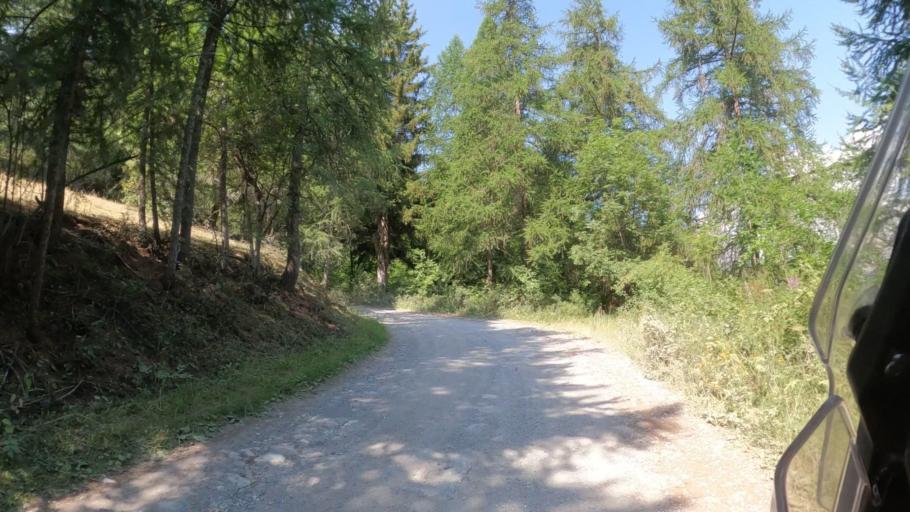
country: IT
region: Piedmont
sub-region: Provincia di Torino
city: Cesana Torinese
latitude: 44.9326
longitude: 6.8130
